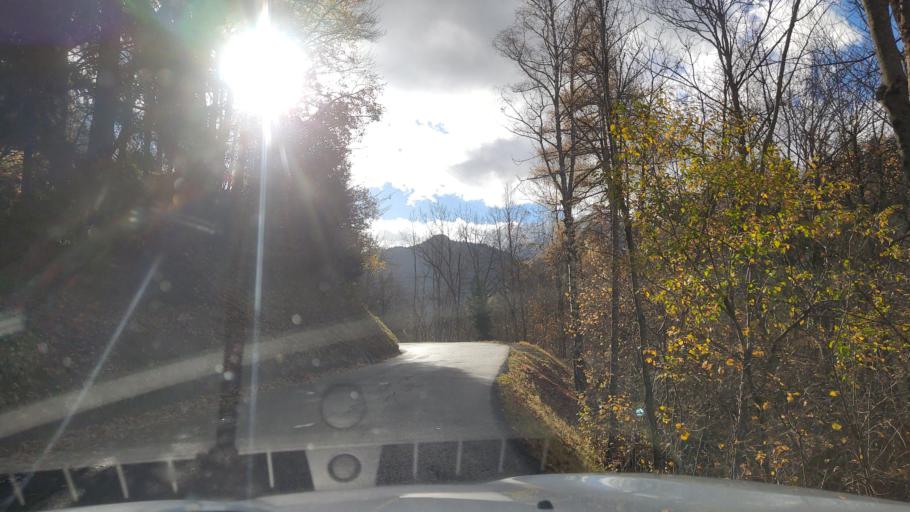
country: FR
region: Rhone-Alpes
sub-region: Departement de la Savoie
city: Saint-Jean-de-Maurienne
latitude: 45.2223
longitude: 6.3182
